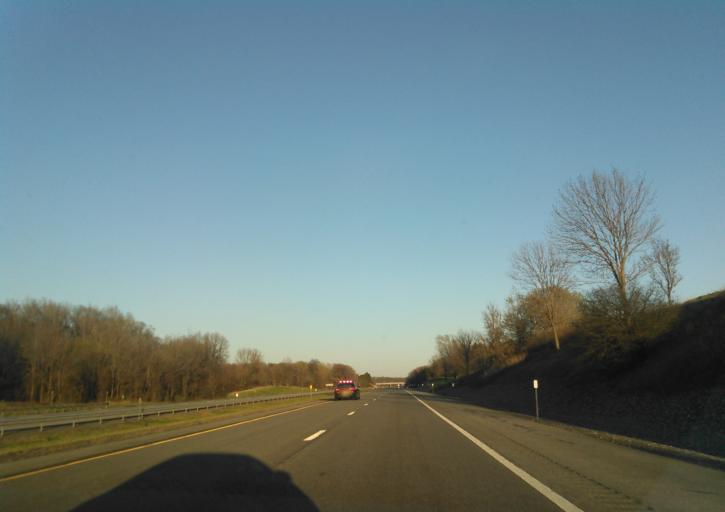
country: US
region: New York
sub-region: Monroe County
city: Pittsford
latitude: 43.0387
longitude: -77.5380
